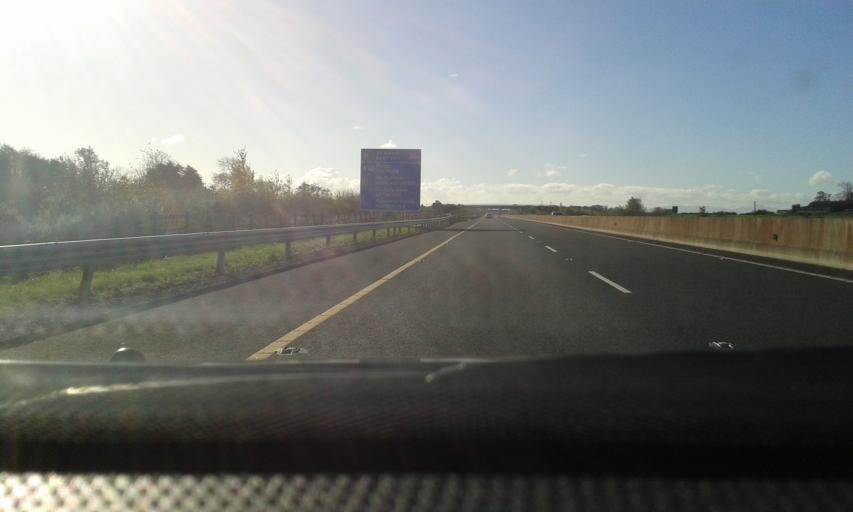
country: IE
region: Munster
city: Thurles
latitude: 52.6427
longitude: -7.7558
